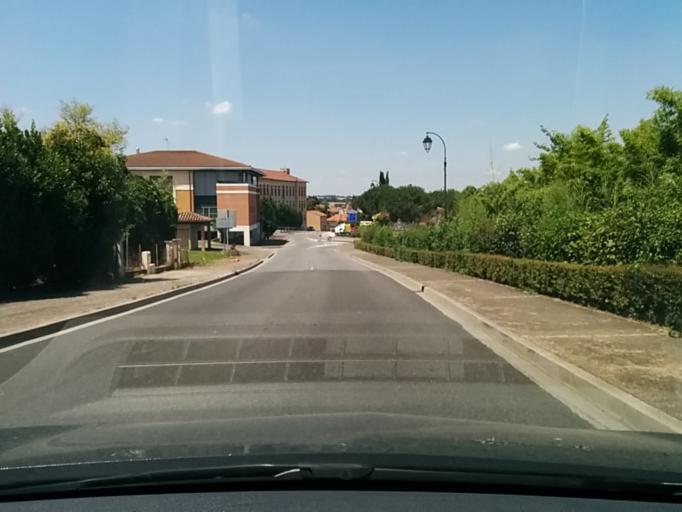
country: FR
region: Midi-Pyrenees
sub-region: Departement du Gers
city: Gimont
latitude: 43.6239
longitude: 0.8819
